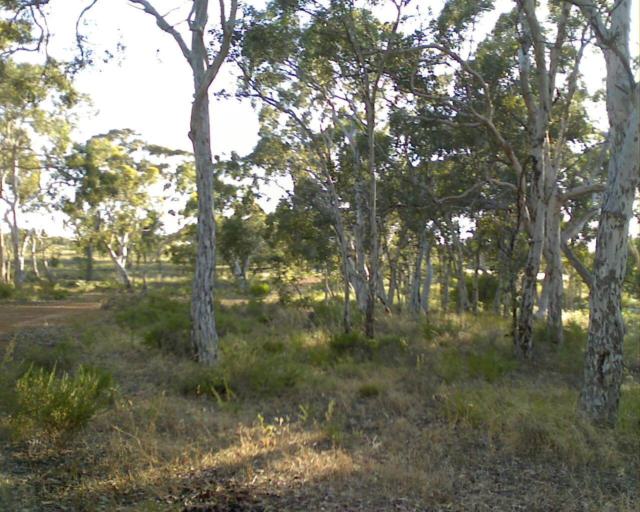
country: AU
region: Western Australia
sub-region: Dandaragan
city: Jurien Bay
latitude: -30.0631
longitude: 115.1787
